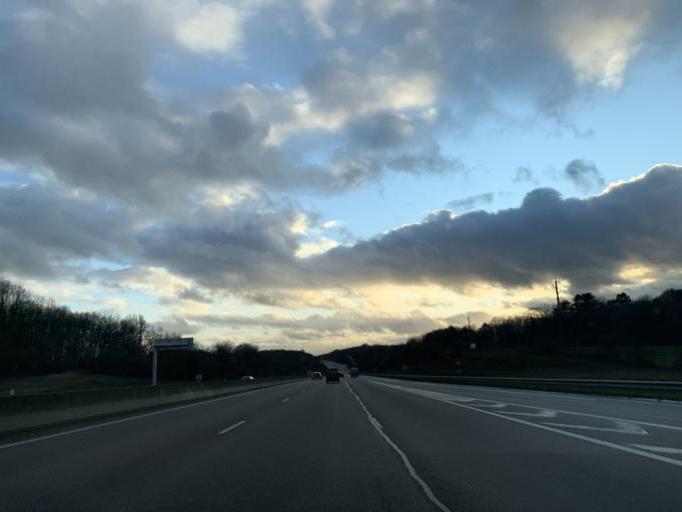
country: FR
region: Bourgogne
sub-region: Departement de la Cote-d'Or
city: Selongey
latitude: 47.6873
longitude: 5.1822
